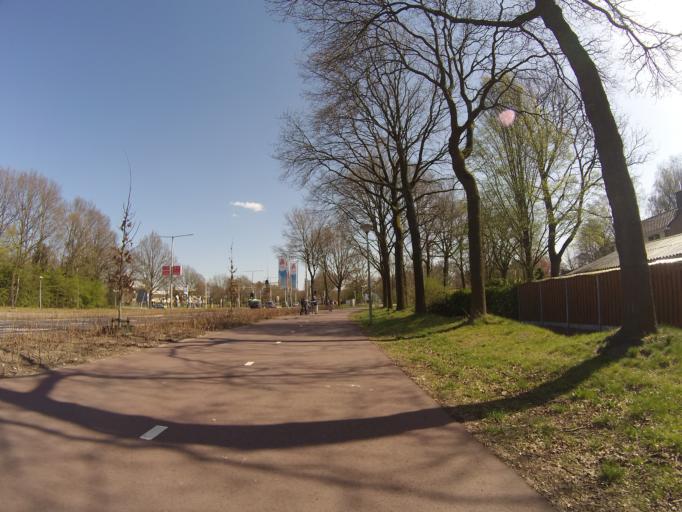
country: NL
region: Utrecht
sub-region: Gemeente Amersfoort
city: Hoogland
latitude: 52.1703
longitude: 5.3729
